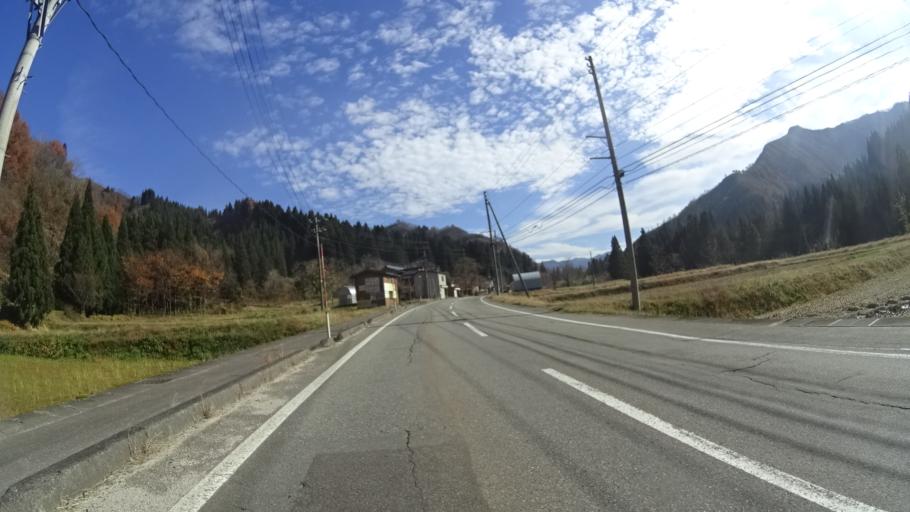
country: JP
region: Niigata
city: Muikamachi
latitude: 37.2247
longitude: 139.0206
